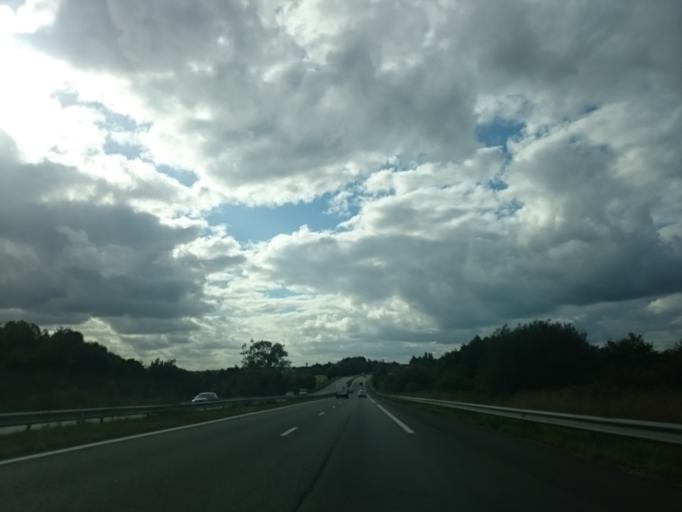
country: FR
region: Brittany
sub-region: Departement d'Ille-et-Vilaine
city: Montauban-de-Bretagne
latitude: 48.1860
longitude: -1.9968
